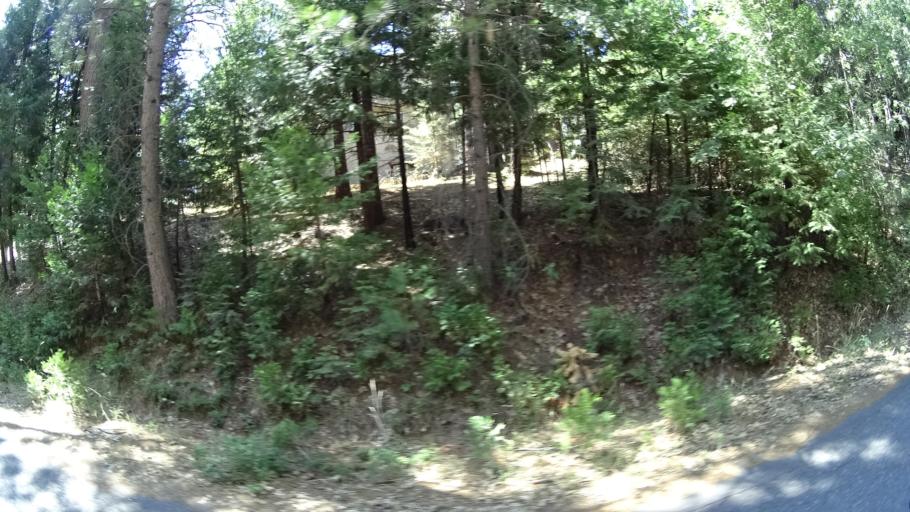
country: US
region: California
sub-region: Calaveras County
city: Arnold
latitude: 38.2415
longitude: -120.3383
